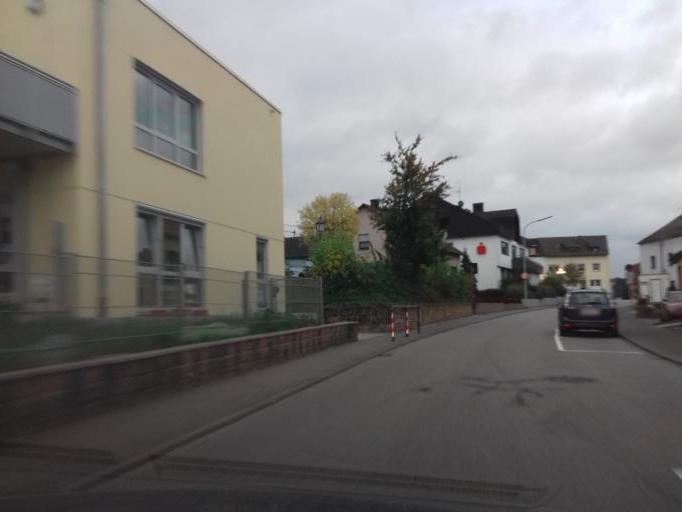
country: DE
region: Rheinland-Pfalz
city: Tawern
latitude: 49.6723
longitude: 6.5210
